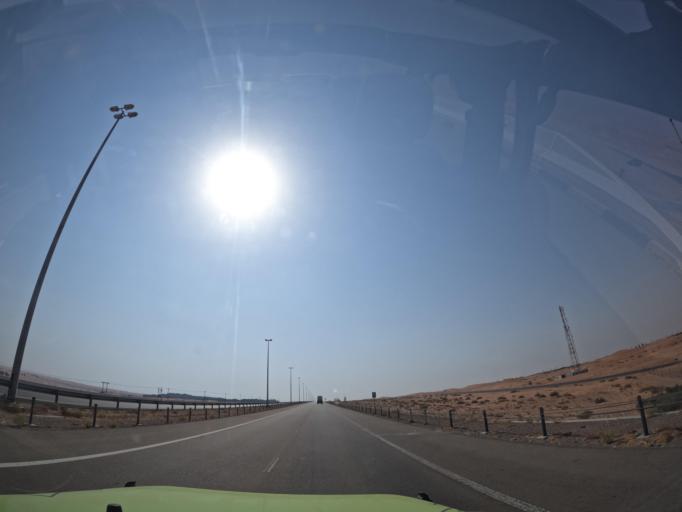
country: OM
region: Al Buraimi
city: Al Buraymi
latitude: 24.4211
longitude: 55.6887
